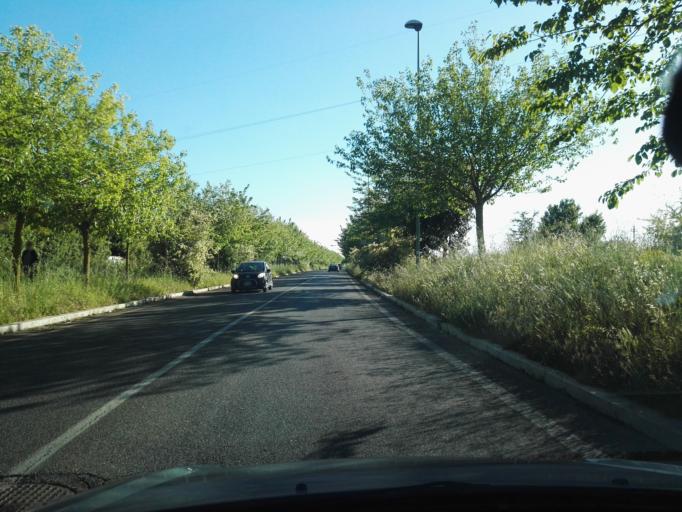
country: IT
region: Latium
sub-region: Citta metropolitana di Roma Capitale
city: Selcetta
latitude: 41.7817
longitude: 12.4758
